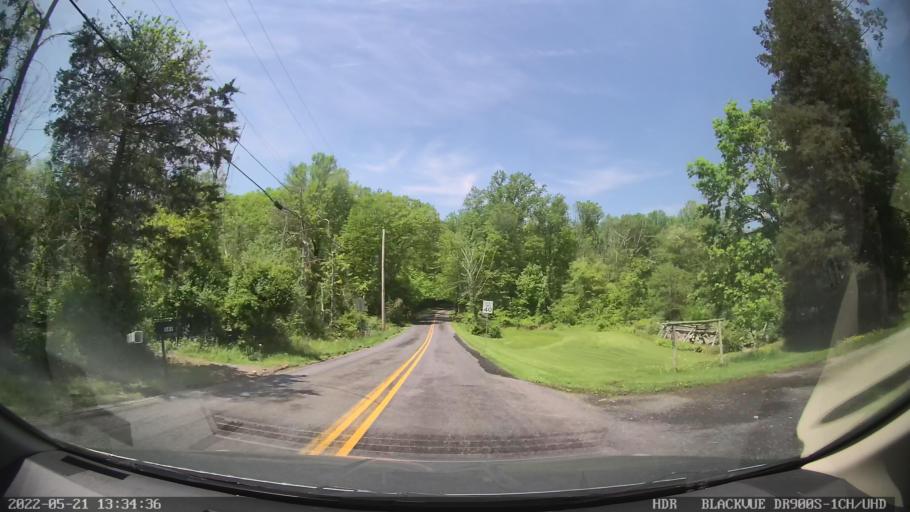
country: US
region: Pennsylvania
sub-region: Berks County
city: Topton
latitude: 40.4428
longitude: -75.6767
